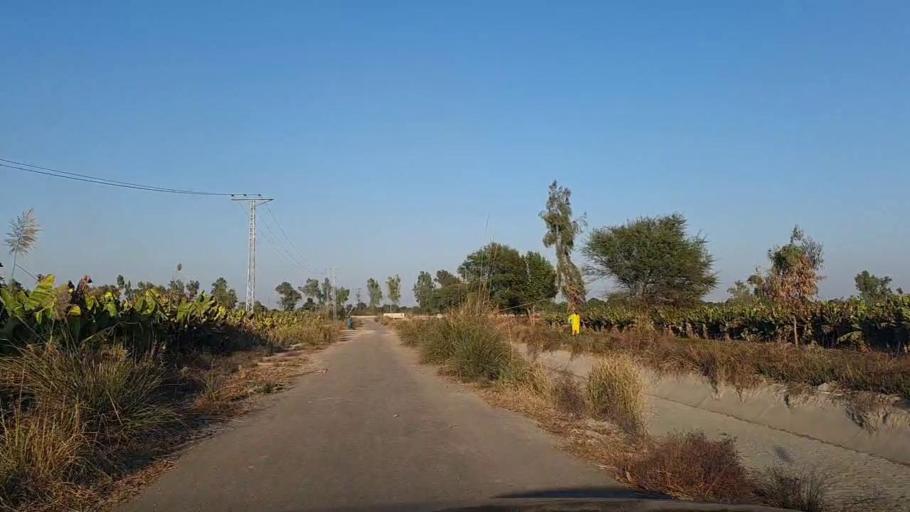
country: PK
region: Sindh
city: Sakrand
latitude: 26.2345
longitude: 68.2796
